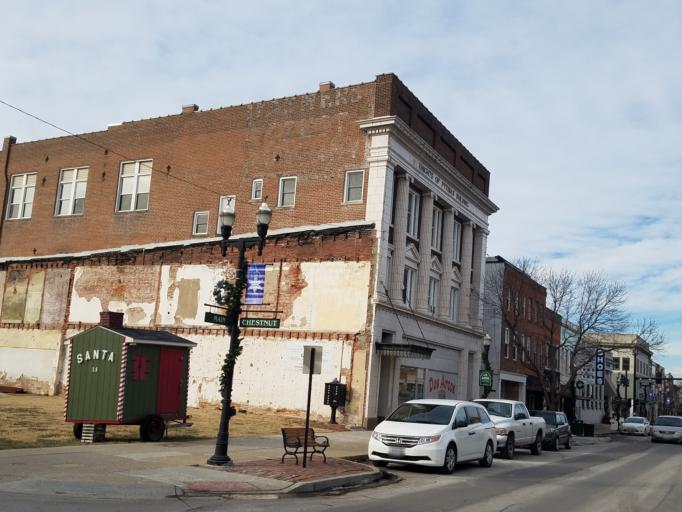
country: US
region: Missouri
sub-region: Cooper County
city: Boonville
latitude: 38.9744
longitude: -92.7434
